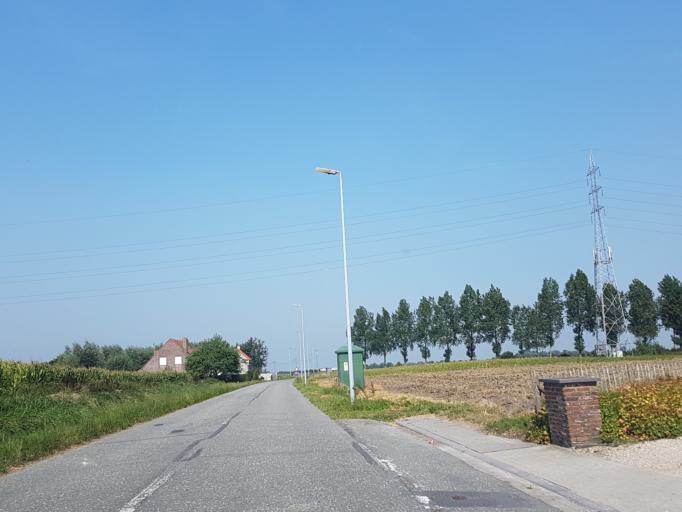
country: BE
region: Flanders
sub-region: Provincie West-Vlaanderen
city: Jabbeke
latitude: 51.2215
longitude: 3.0668
